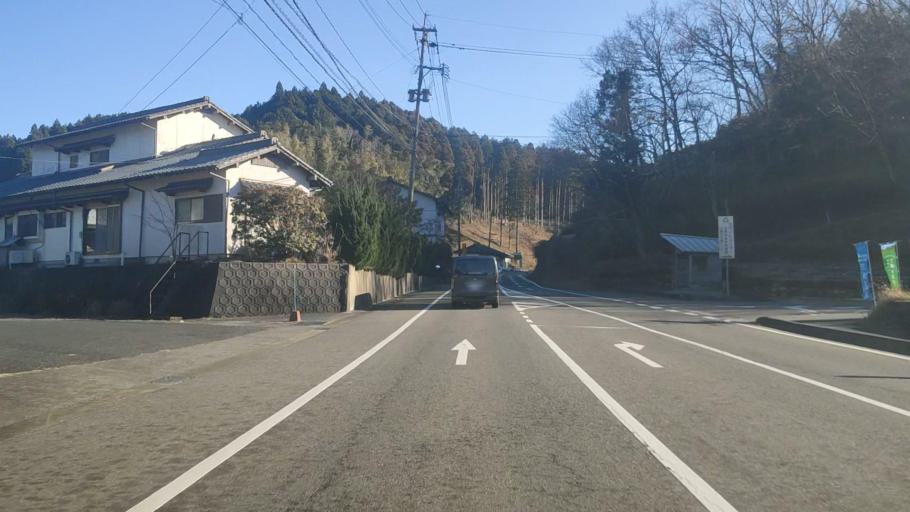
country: JP
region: Saga Prefecture
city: Kanzakimachi-kanzaki
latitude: 33.4214
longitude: 130.2782
